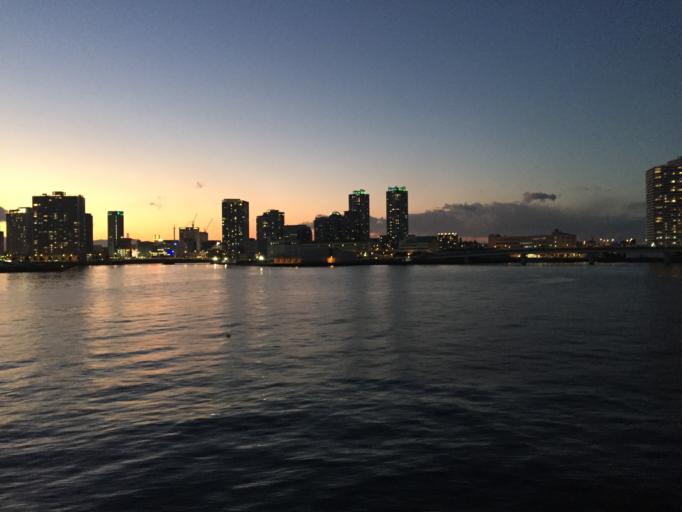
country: JP
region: Kanagawa
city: Yokohama
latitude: 35.4640
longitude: 139.6432
